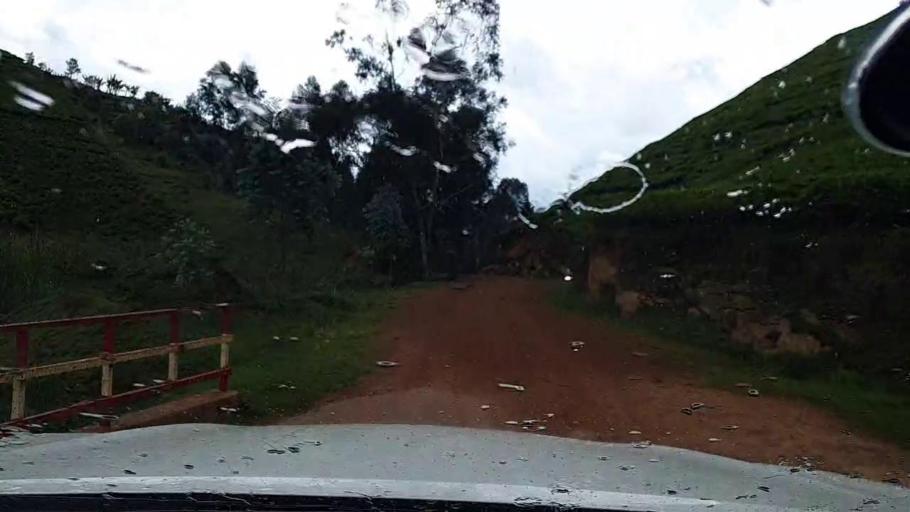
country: RW
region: Western Province
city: Kibuye
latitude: -2.1666
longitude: 29.4357
